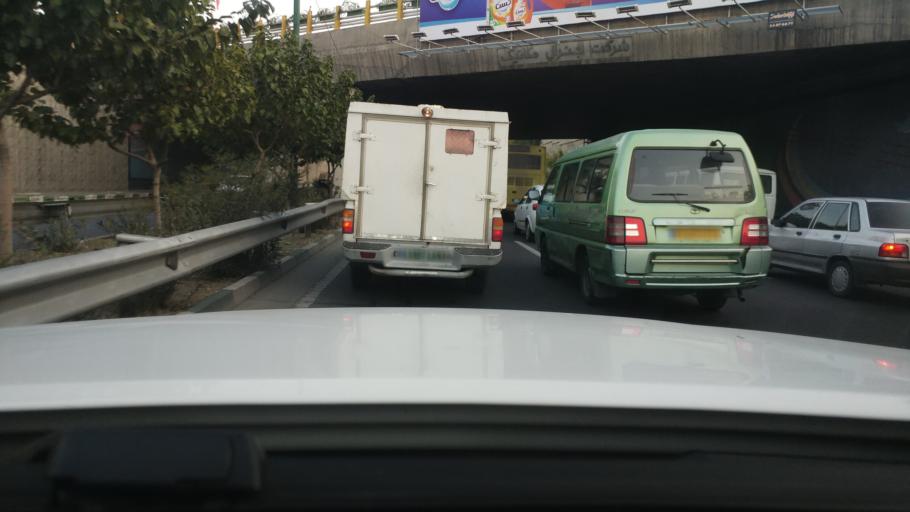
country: IR
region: Tehran
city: Tehran
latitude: 35.7315
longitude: 51.3111
